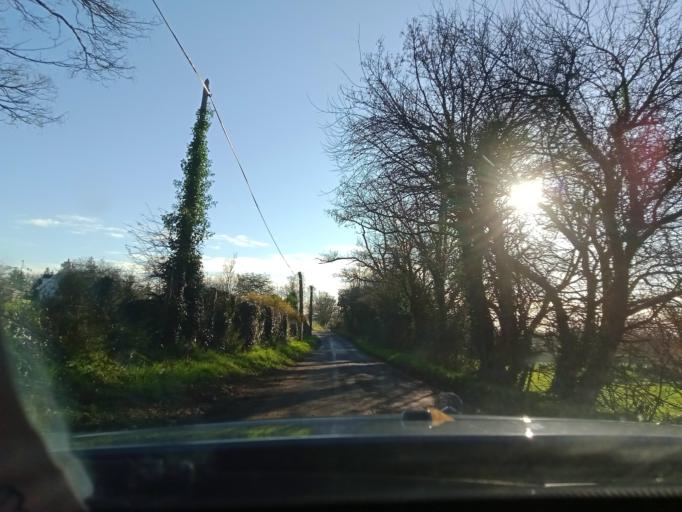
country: IE
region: Leinster
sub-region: Kilkenny
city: Mooncoin
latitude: 52.3364
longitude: -7.2636
